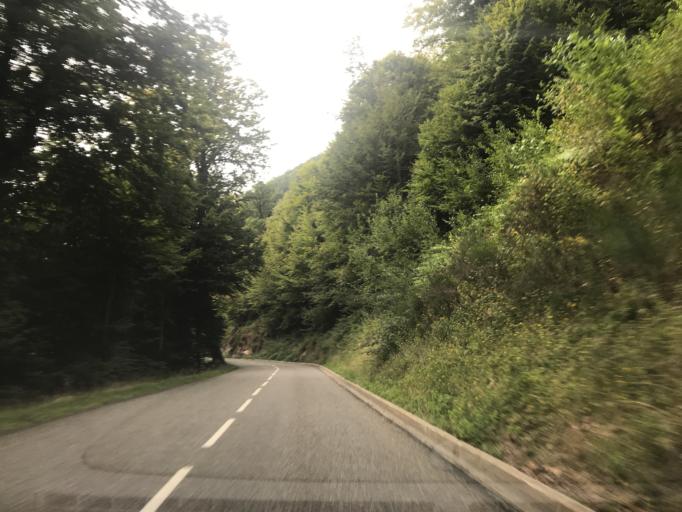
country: FR
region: Midi-Pyrenees
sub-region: Departement de la Haute-Garonne
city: Bagneres-de-Luchon
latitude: 42.7713
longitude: 0.6490
